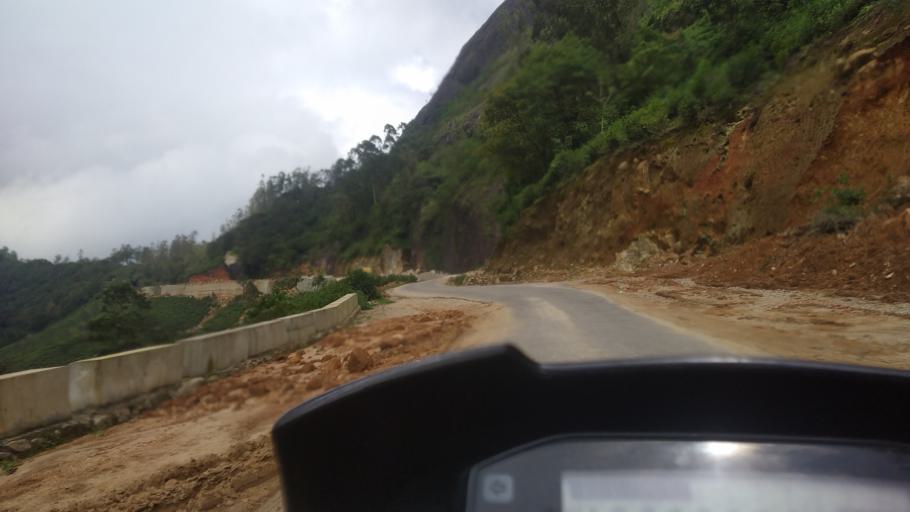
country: IN
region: Kerala
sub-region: Idukki
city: Munnar
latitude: 10.0367
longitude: 77.1164
